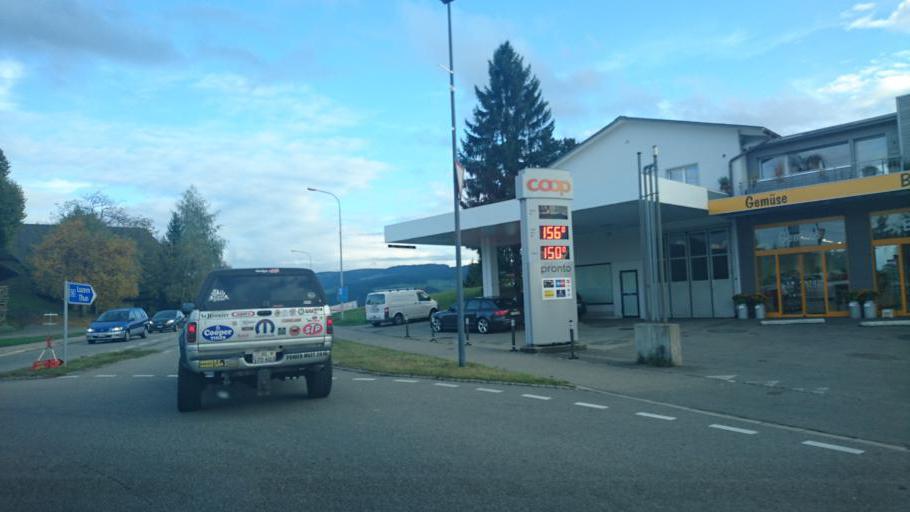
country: CH
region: Bern
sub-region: Bern-Mittelland District
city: Biglen
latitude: 46.9103
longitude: 7.6325
